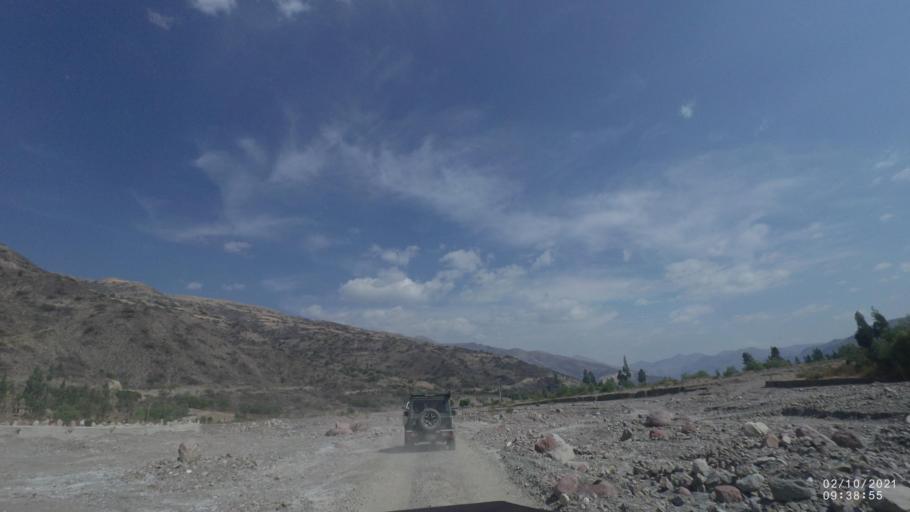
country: BO
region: Cochabamba
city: Irpa Irpa
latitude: -17.8266
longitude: -66.3263
